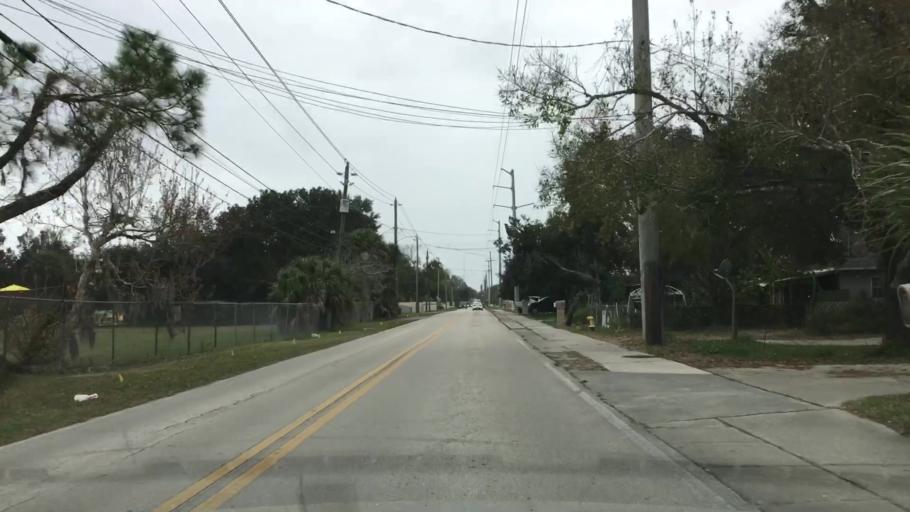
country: US
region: Florida
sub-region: Volusia County
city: Holly Hill
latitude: 29.2446
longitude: -81.0543
